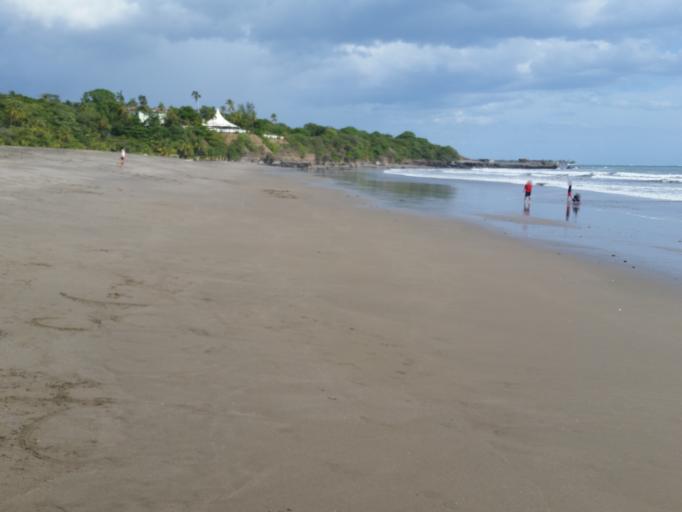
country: NI
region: Managua
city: Masachapa
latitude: 11.8071
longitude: -86.5221
